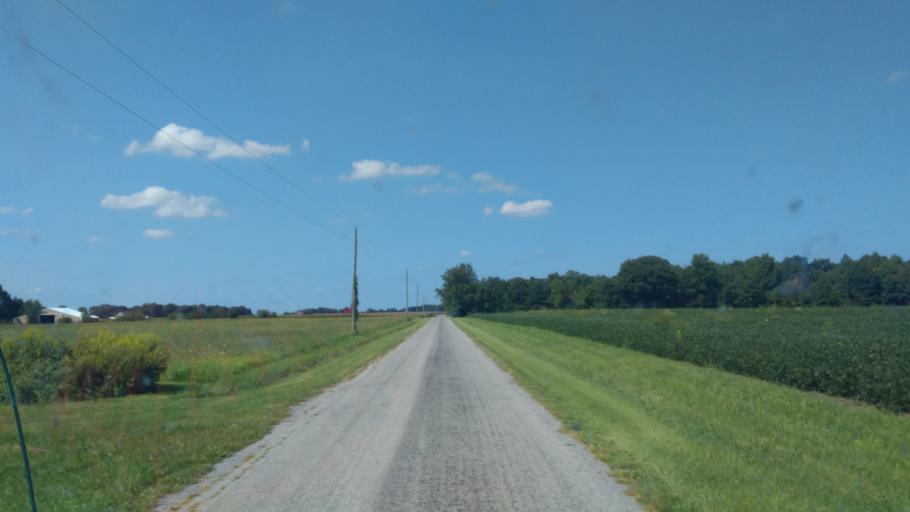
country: US
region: Ohio
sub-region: Union County
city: Richwood
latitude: 40.4965
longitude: -83.3953
